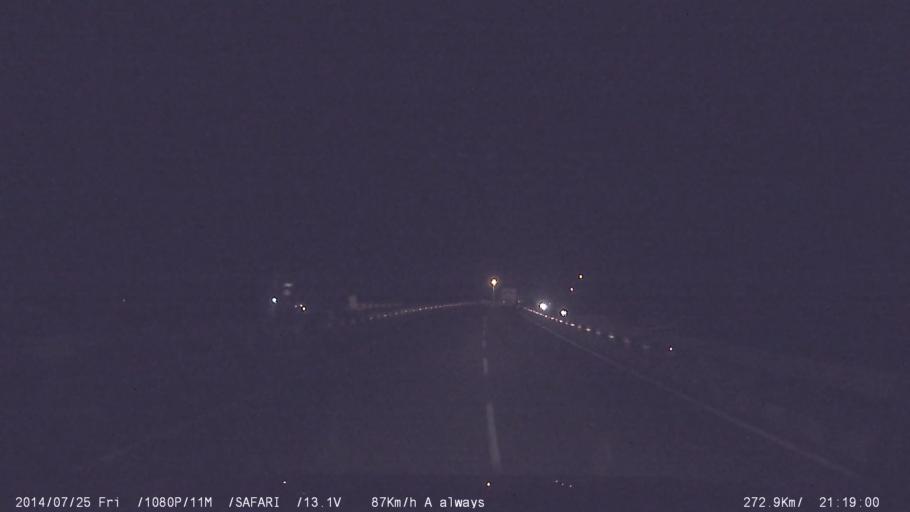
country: IN
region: Tamil Nadu
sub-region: Erode
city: Perundurai
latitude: 11.2996
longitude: 77.5992
